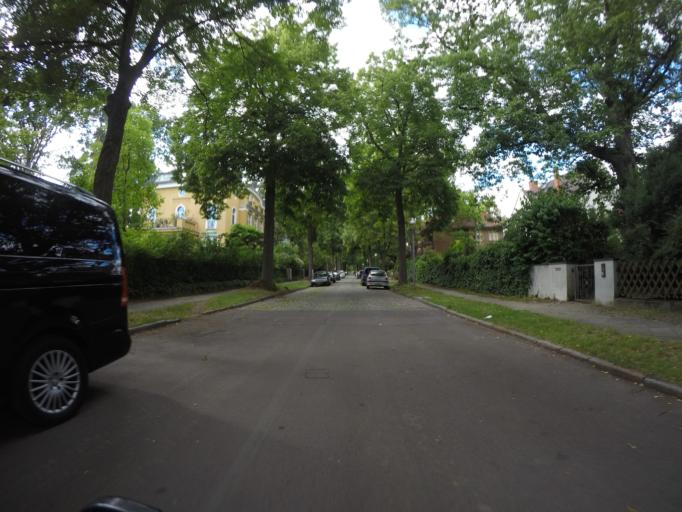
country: DE
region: Berlin
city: Zehlendorf Bezirk
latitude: 52.4258
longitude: 13.2660
